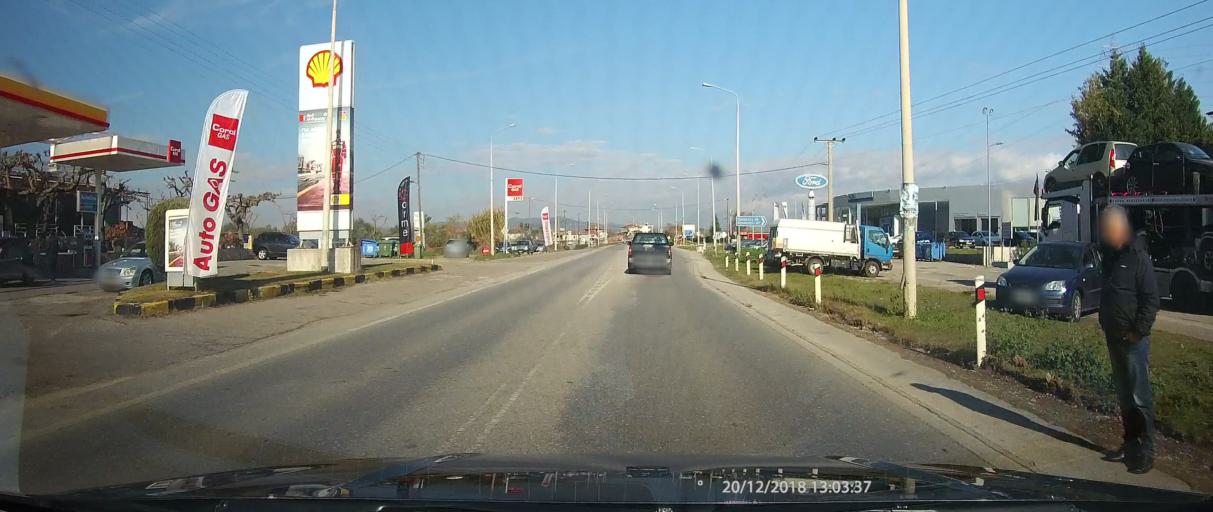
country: GR
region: West Greece
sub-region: Nomos Aitolias kai Akarnanias
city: Panaitolion
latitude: 38.5831
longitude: 21.4274
